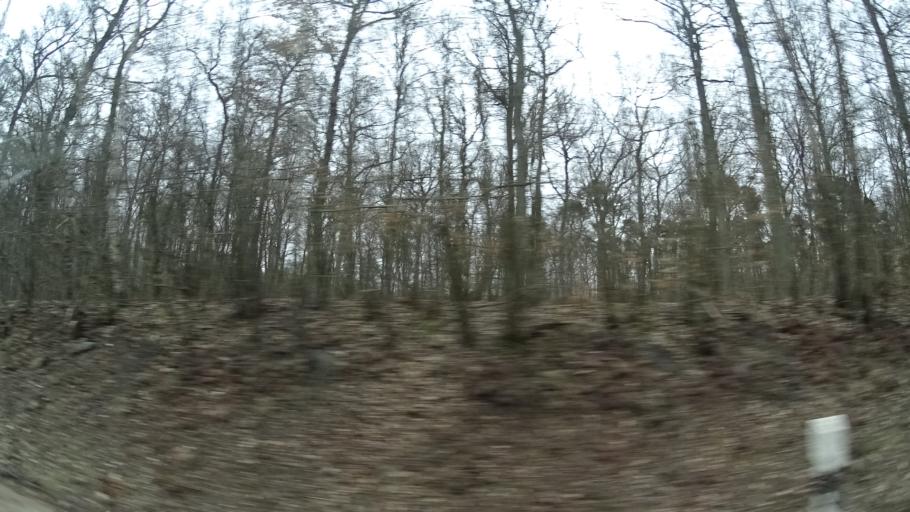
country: DE
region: Rheinland-Pfalz
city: Oberwiesen
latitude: 49.6719
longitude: 7.9798
